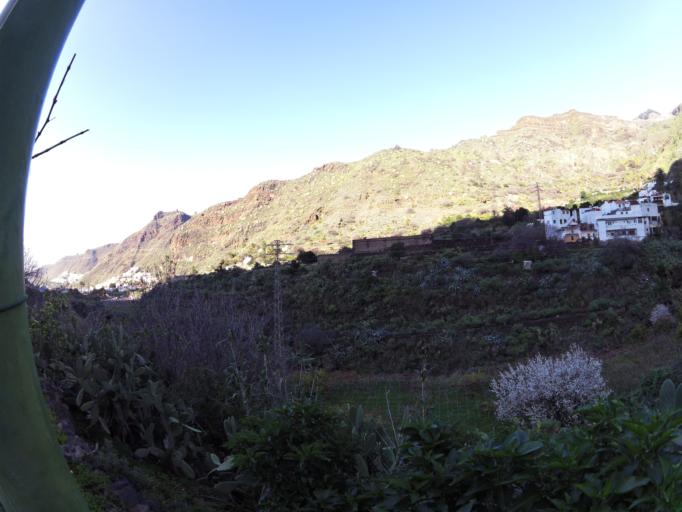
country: ES
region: Canary Islands
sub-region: Provincia de Las Palmas
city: Agaete
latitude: 28.0756
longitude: -15.6689
